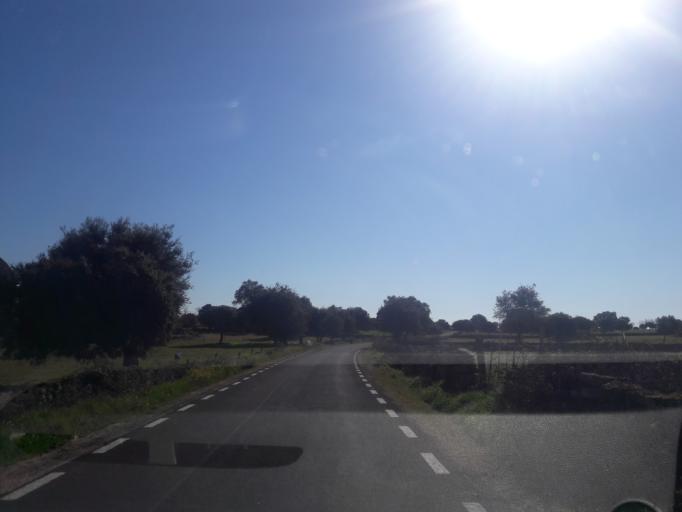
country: ES
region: Castille and Leon
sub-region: Provincia de Salamanca
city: Cabeza del Caballo
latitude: 41.1746
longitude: -6.5149
